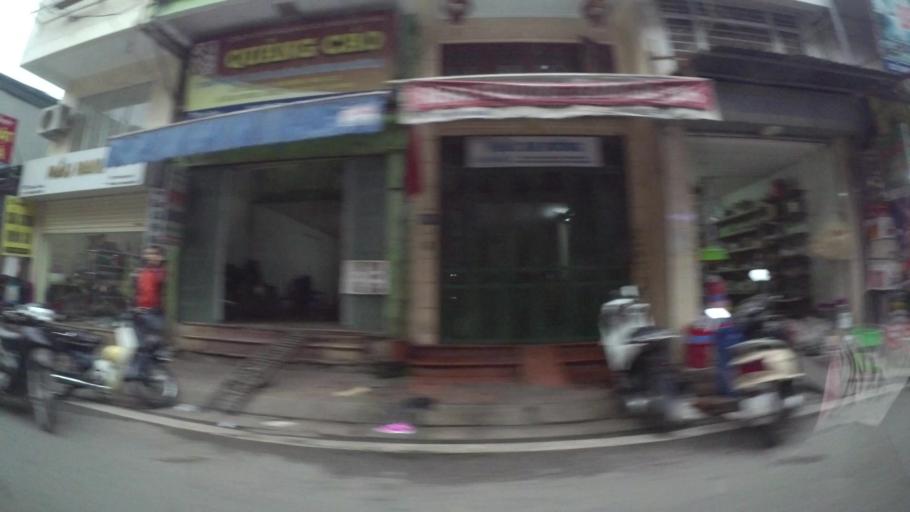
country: VN
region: Ha Noi
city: Hoan Kiem
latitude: 21.0183
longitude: 105.8643
